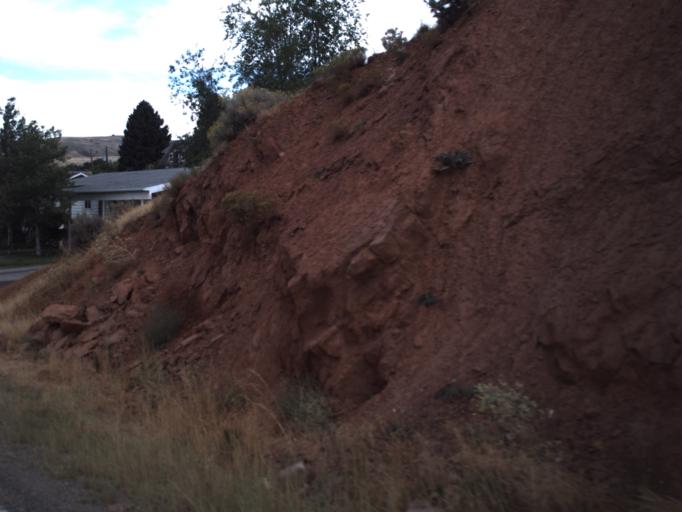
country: US
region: Utah
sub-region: Morgan County
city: Morgan
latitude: 41.0472
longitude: -111.6719
